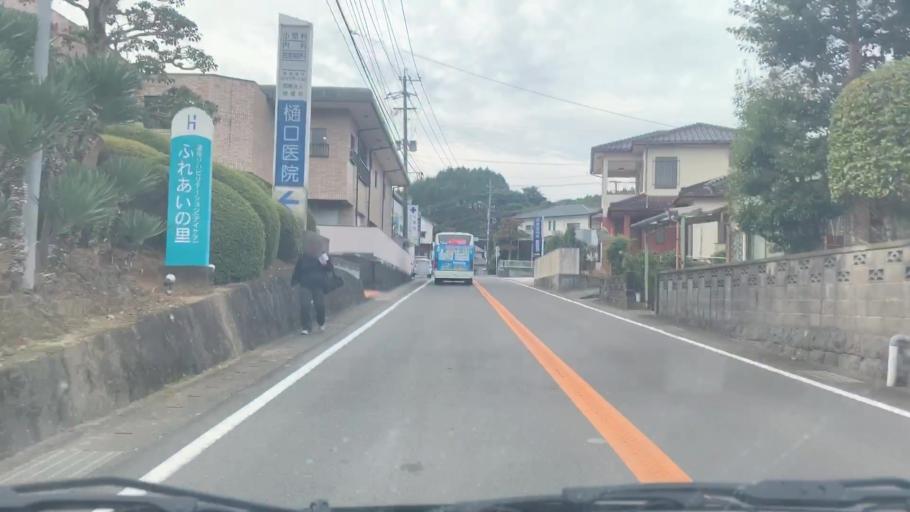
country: JP
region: Saga Prefecture
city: Ureshinomachi-shimojuku
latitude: 33.1201
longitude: 130.0015
